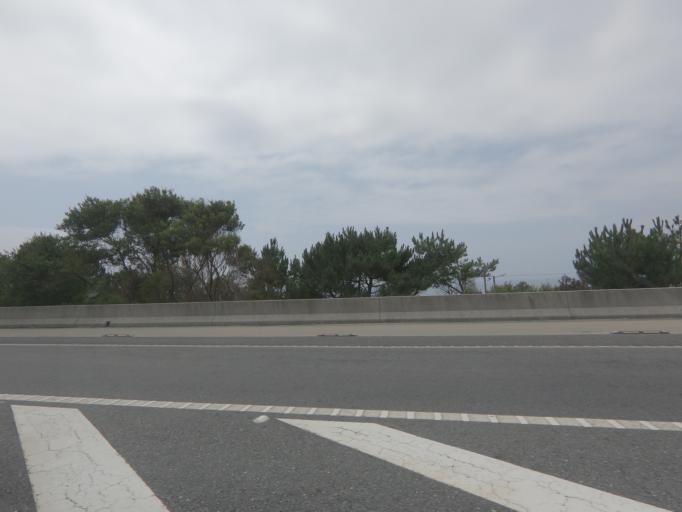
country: ES
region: Galicia
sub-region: Provincia de Pontevedra
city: Oia
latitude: 41.9864
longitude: -8.8841
